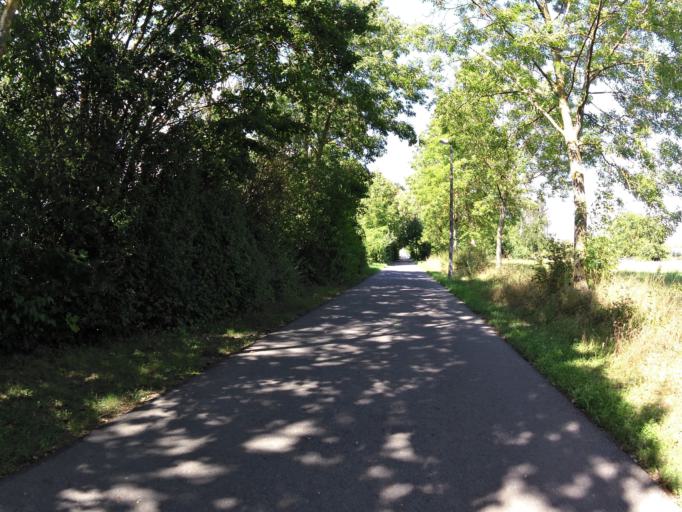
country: DE
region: Bavaria
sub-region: Regierungsbezirk Unterfranken
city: Kitzingen
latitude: 49.7305
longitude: 10.1692
